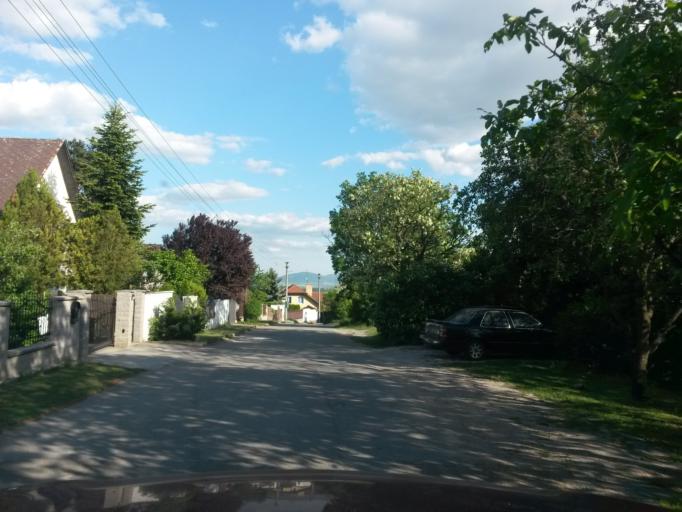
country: SK
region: Kosicky
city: Kosice
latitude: 48.6845
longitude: 21.2118
